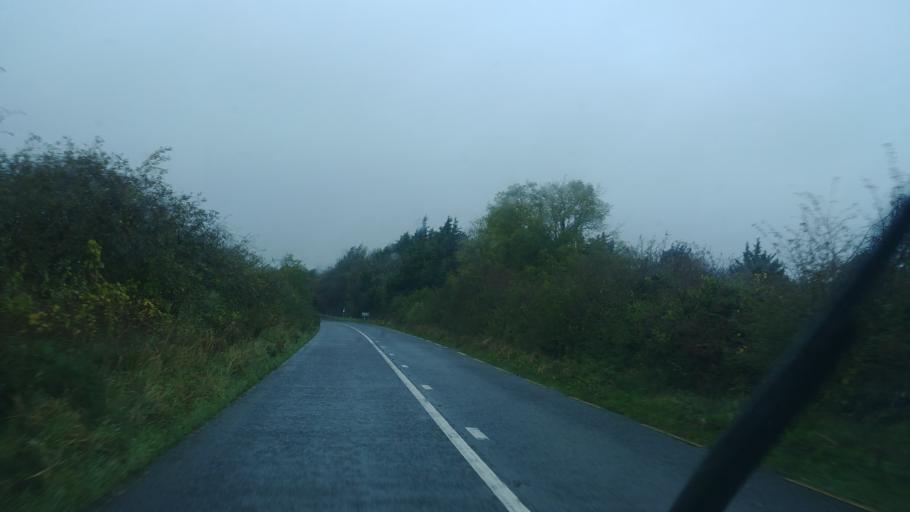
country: IE
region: Connaught
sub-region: Roscommon
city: Ballaghaderreen
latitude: 53.9096
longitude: -8.5955
